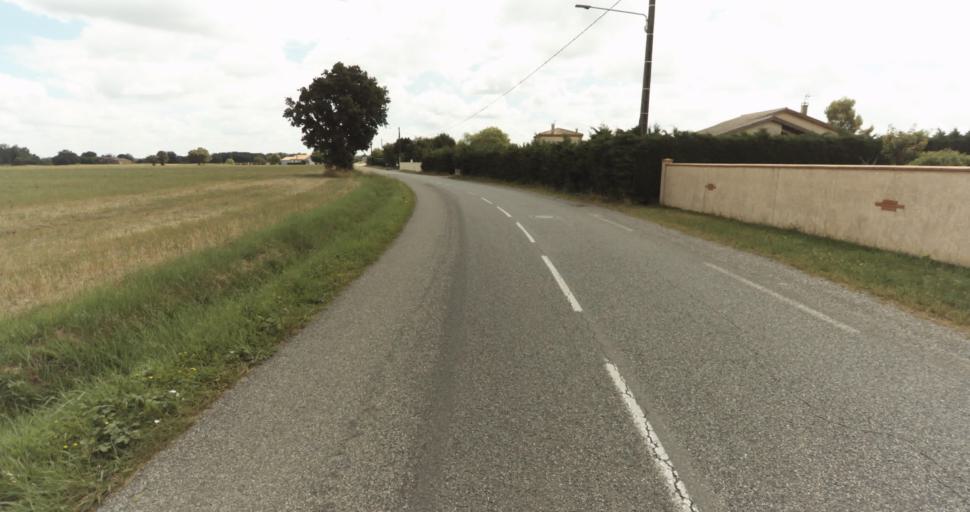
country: FR
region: Midi-Pyrenees
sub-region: Departement de la Haute-Garonne
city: Fontenilles
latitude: 43.5576
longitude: 1.1877
